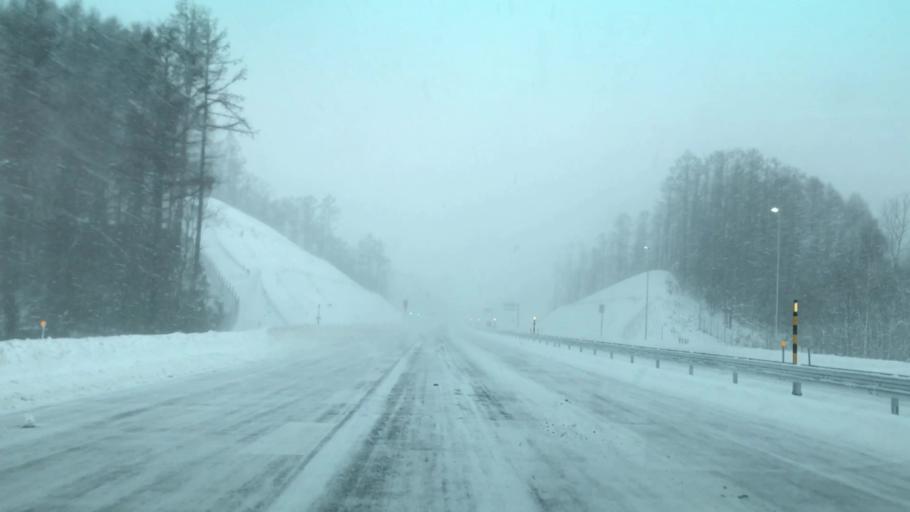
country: JP
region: Hokkaido
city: Otaru
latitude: 43.1982
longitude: 140.9252
